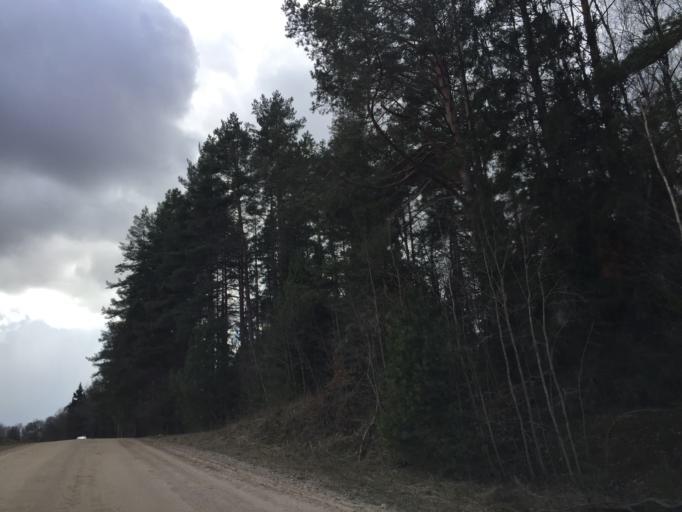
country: LV
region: Akniste
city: Akniste
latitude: 56.1088
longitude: 25.8291
